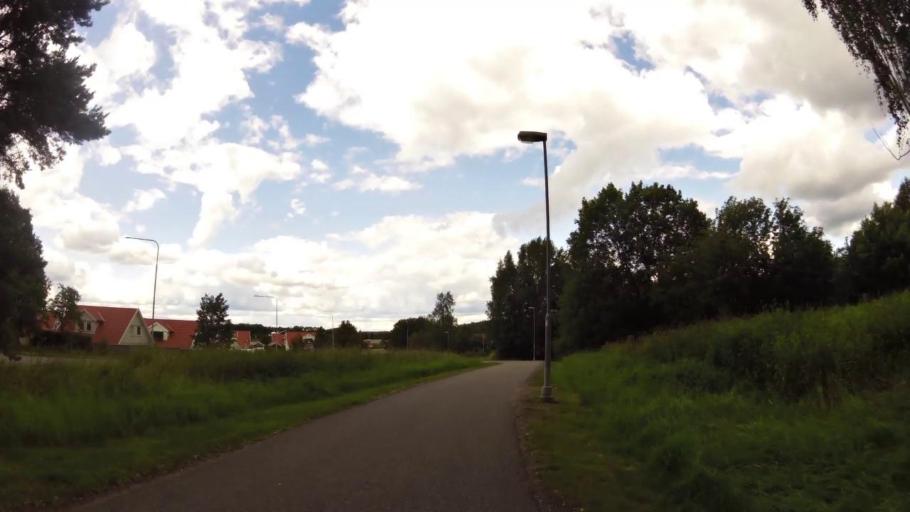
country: SE
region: OEstergoetland
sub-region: Linkopings Kommun
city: Ekangen
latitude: 58.4292
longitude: 15.6767
